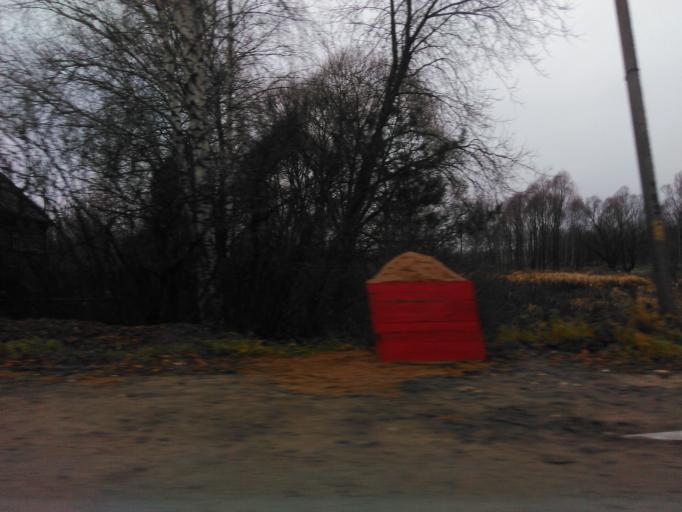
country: RU
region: Moskovskaya
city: Sofrino
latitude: 56.1236
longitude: 37.9675
